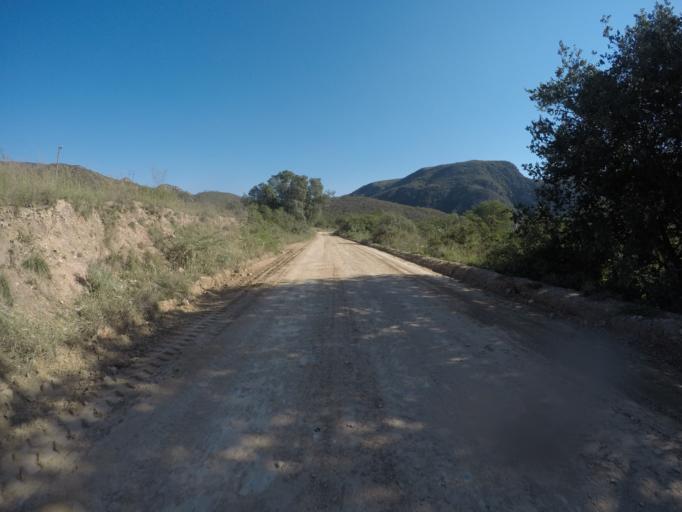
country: ZA
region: Eastern Cape
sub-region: Cacadu District Municipality
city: Kareedouw
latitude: -33.6642
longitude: 24.5422
